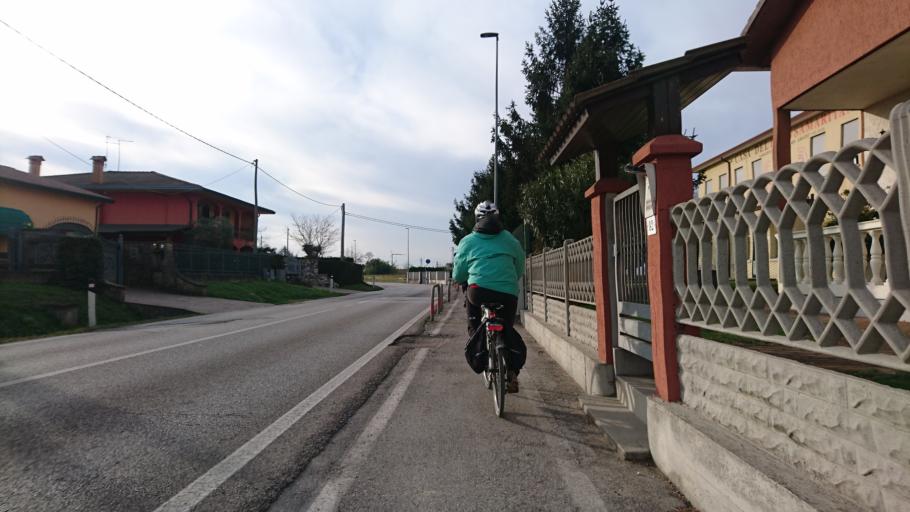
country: IT
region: Veneto
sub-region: Provincia di Padova
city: Polverara
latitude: 45.3215
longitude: 11.9631
